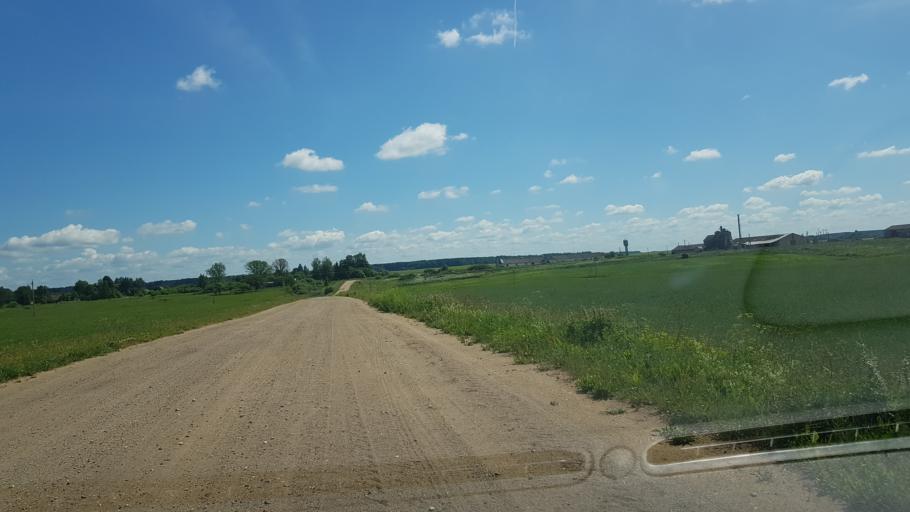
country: BY
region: Vitebsk
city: Dubrowna
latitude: 54.4825
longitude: 30.7927
